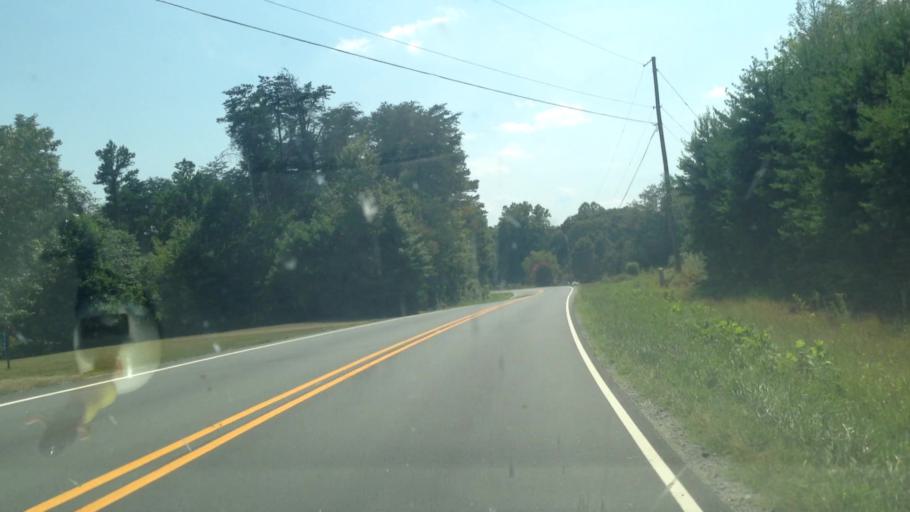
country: US
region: North Carolina
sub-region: Stokes County
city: Danbury
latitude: 36.4129
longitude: -80.0881
